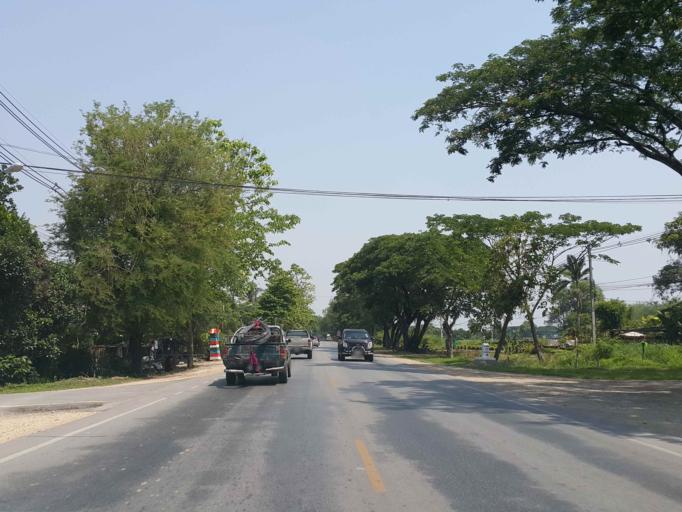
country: TH
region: Chiang Mai
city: San Sai
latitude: 18.9296
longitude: 98.9902
